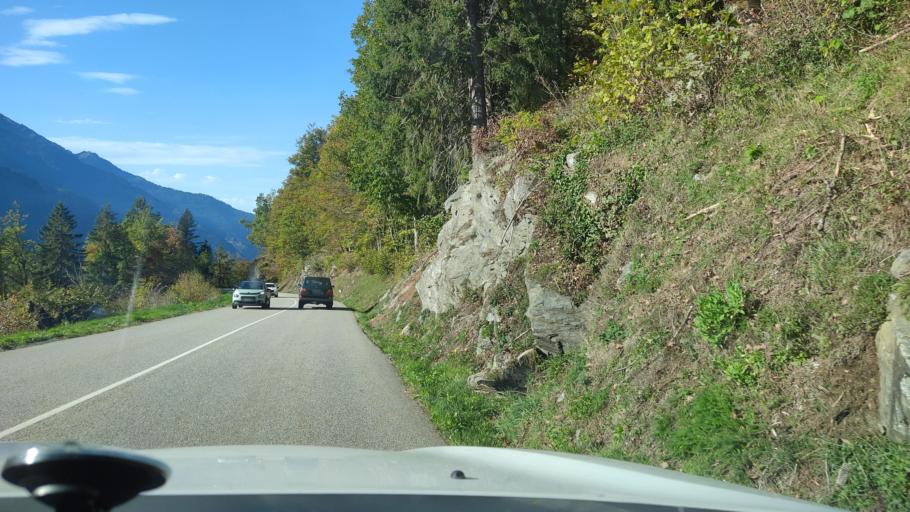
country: FR
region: Rhone-Alpes
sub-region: Departement de la Savoie
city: Beaufort
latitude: 45.7322
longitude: 6.5451
